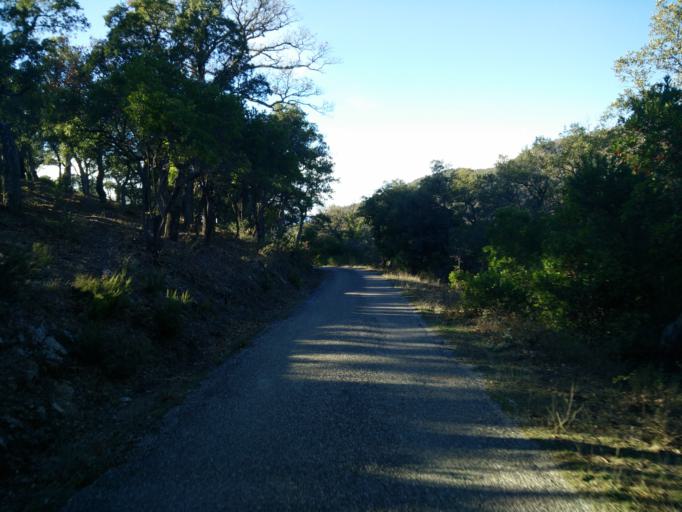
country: FR
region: Provence-Alpes-Cote d'Azur
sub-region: Departement du Var
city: Collobrieres
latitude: 43.2711
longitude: 6.2999
